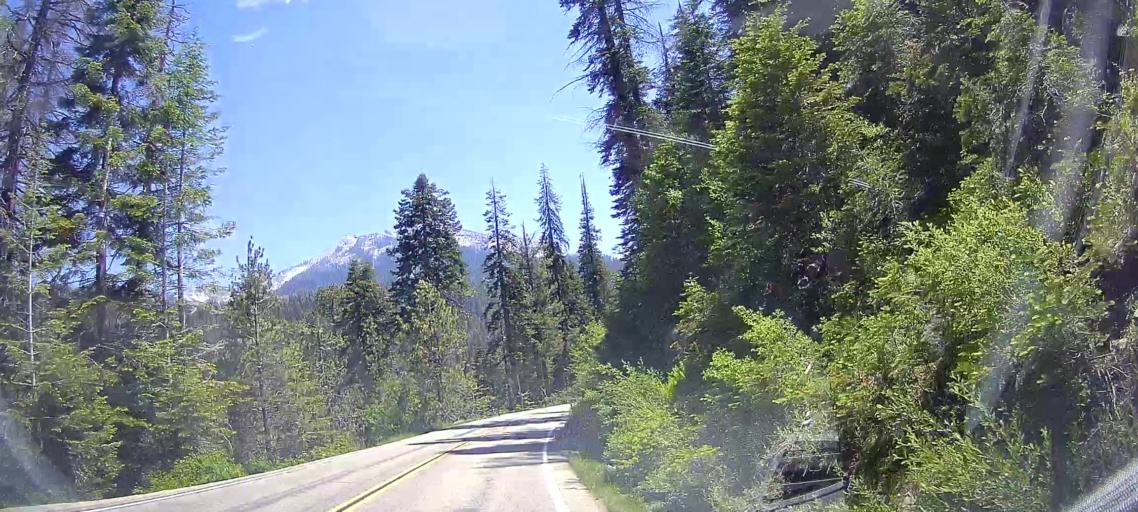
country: US
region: California
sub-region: Tulare County
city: Three Rivers
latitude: 36.6014
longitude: -118.7424
